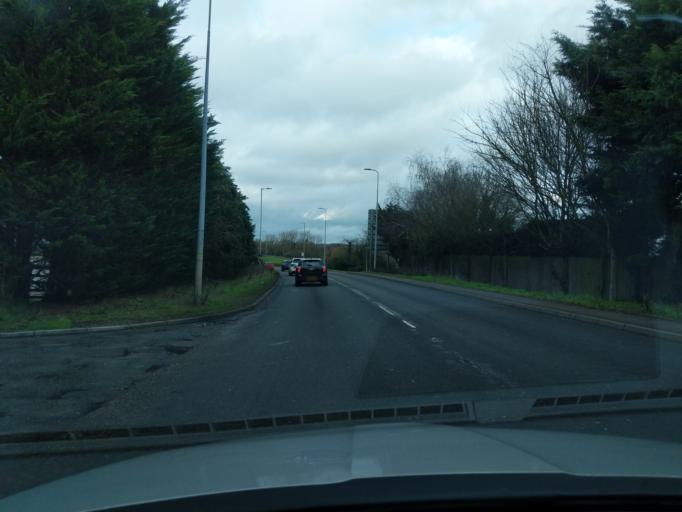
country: GB
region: England
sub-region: Hertfordshire
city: Kings Langley
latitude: 51.7022
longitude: -0.4442
